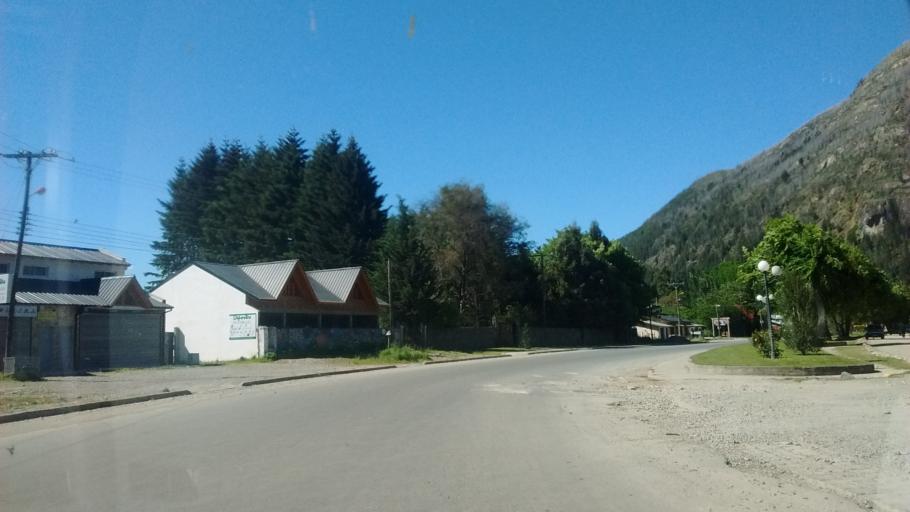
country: AR
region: Chubut
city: Lago Puelo
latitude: -42.0601
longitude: -71.6004
